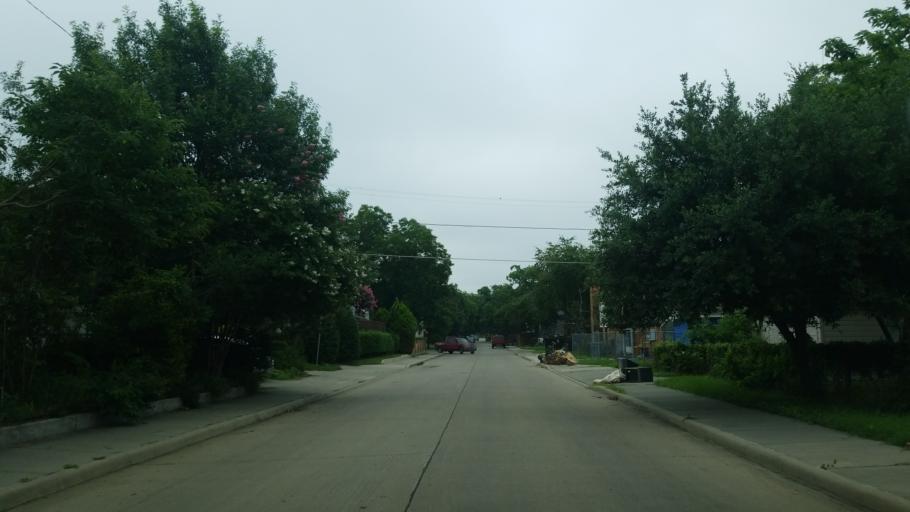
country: US
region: Texas
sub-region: Dallas County
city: University Park
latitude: 32.8374
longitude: -96.8599
